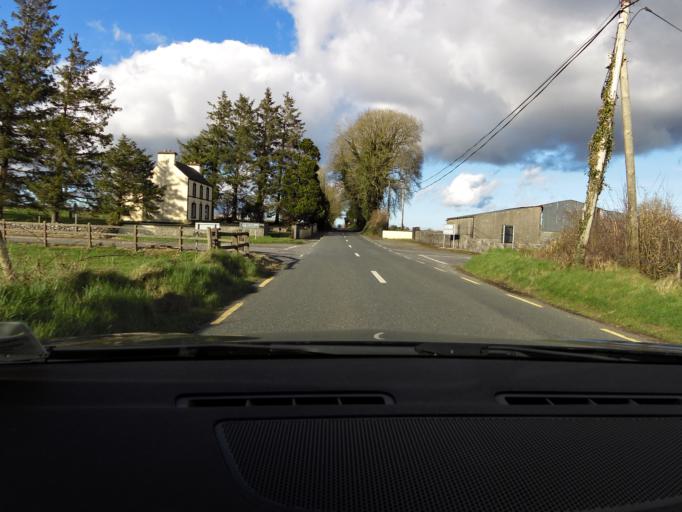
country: IE
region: Connaught
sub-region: Roscommon
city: Castlerea
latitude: 53.6752
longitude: -8.4933
